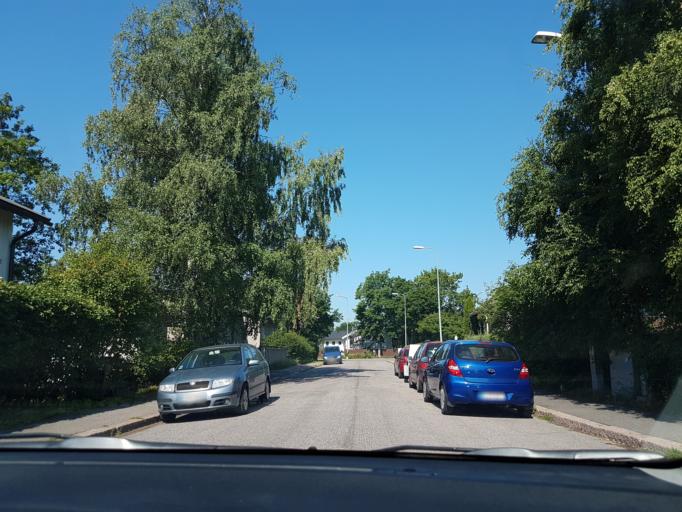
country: FI
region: Uusimaa
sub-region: Helsinki
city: Vantaa
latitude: 60.2558
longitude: 24.9932
